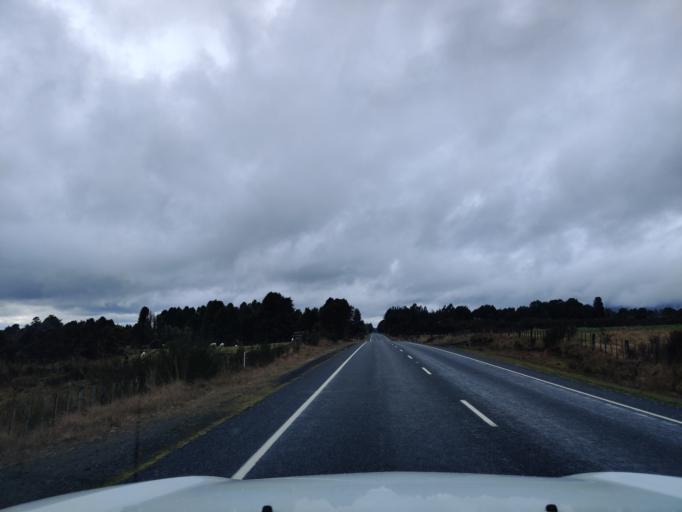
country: NZ
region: Manawatu-Wanganui
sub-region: Ruapehu District
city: Waiouru
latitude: -39.2943
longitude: 175.3876
